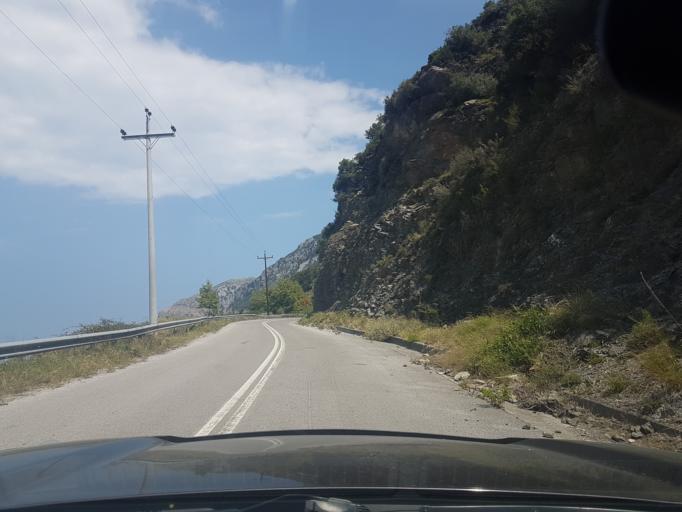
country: GR
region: Central Greece
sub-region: Nomos Evvoias
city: Kymi
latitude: 38.6353
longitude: 23.9547
